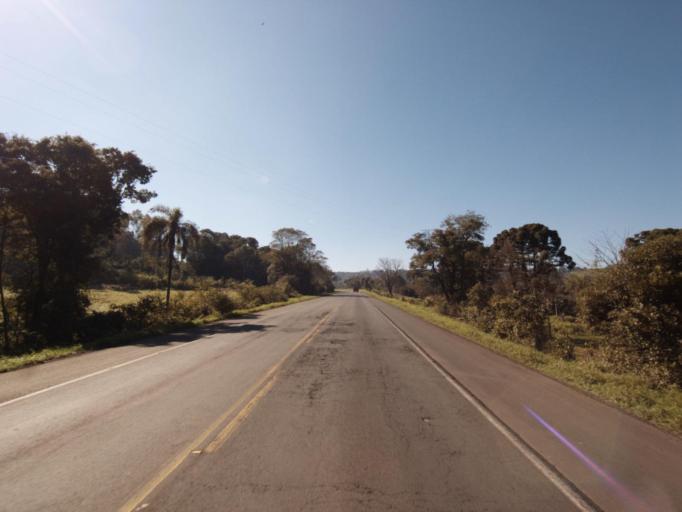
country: BR
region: Rio Grande do Sul
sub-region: Frederico Westphalen
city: Frederico Westphalen
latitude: -27.0667
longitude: -53.2258
